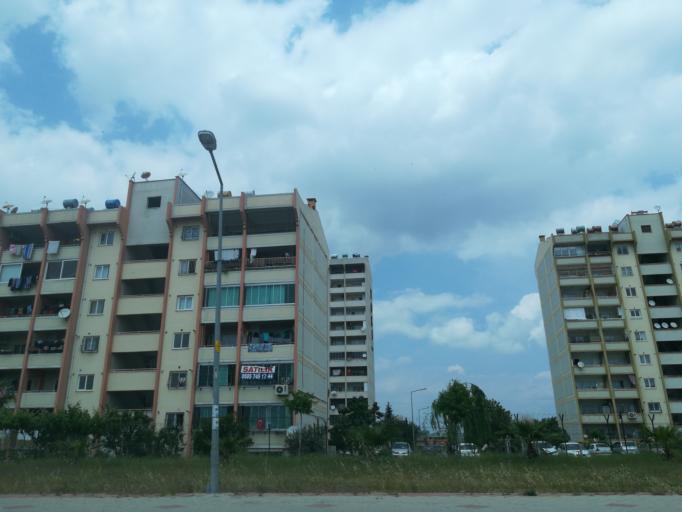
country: TR
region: Adana
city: Seyhan
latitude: 37.0028
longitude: 35.2433
